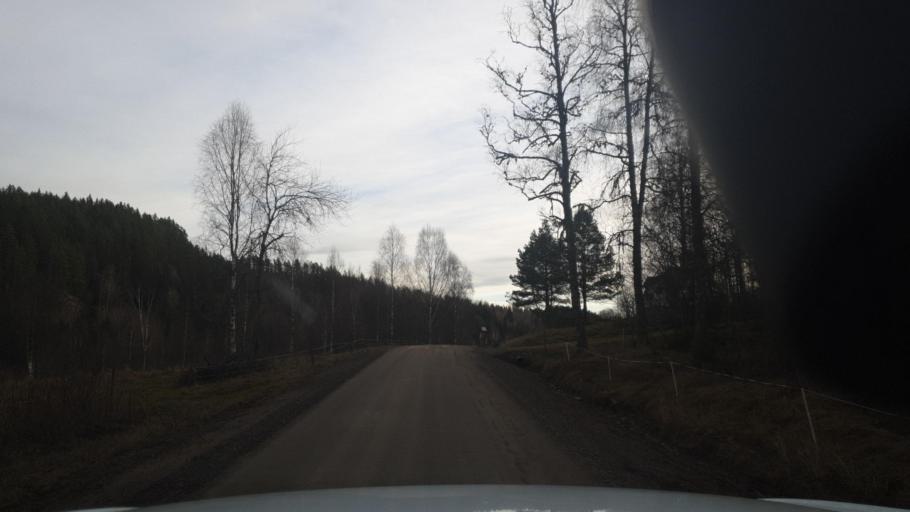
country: NO
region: Hedmark
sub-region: Eidskog
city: Skotterud
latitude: 59.7483
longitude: 12.0637
